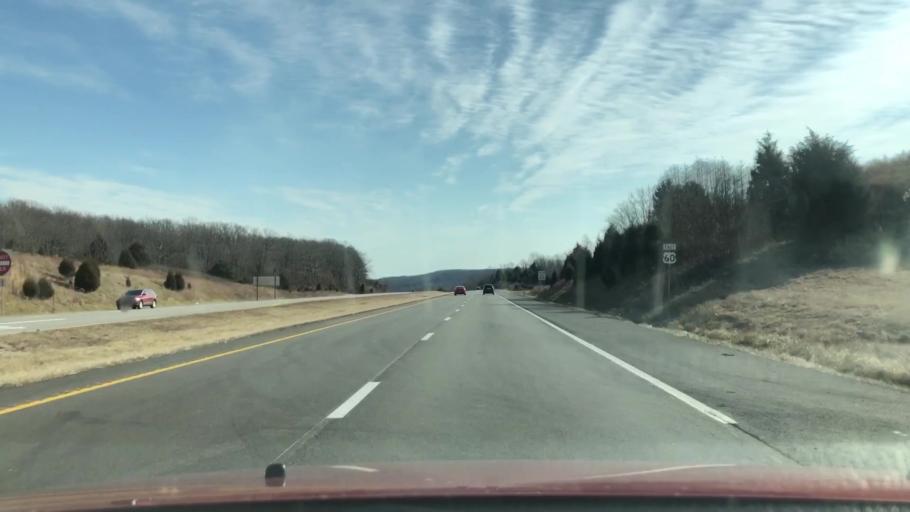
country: US
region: Missouri
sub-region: Wright County
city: Mansfield
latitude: 37.1150
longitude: -92.6747
